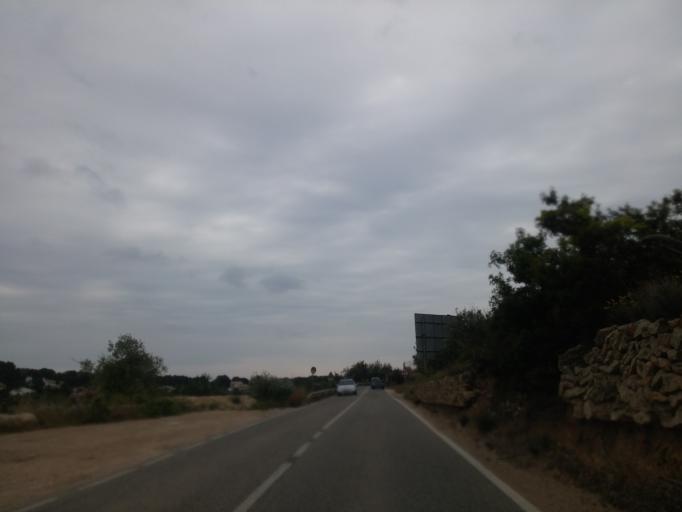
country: ES
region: Valencia
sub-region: Provincia de Alicante
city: Moraira
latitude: 38.6731
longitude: 0.0887
